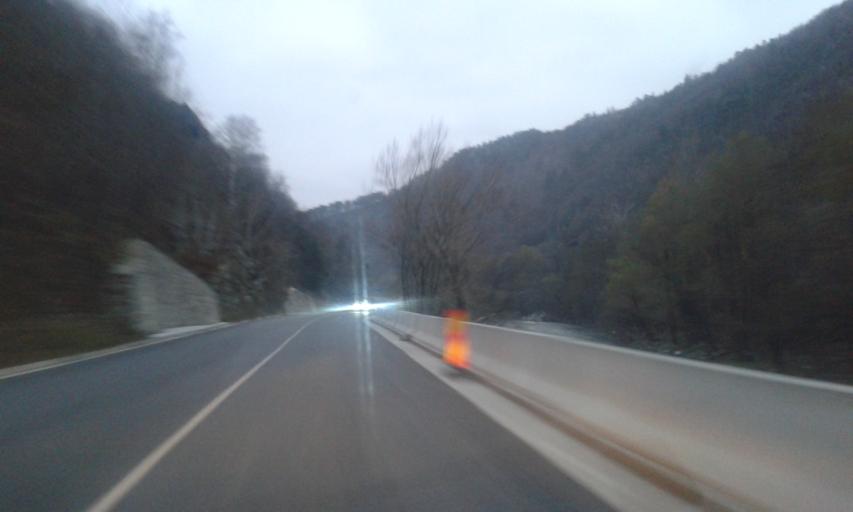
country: RO
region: Gorj
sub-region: Comuna Bumbesti-Jiu
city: Bumbesti-Jiu
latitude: 45.1990
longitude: 23.3805
